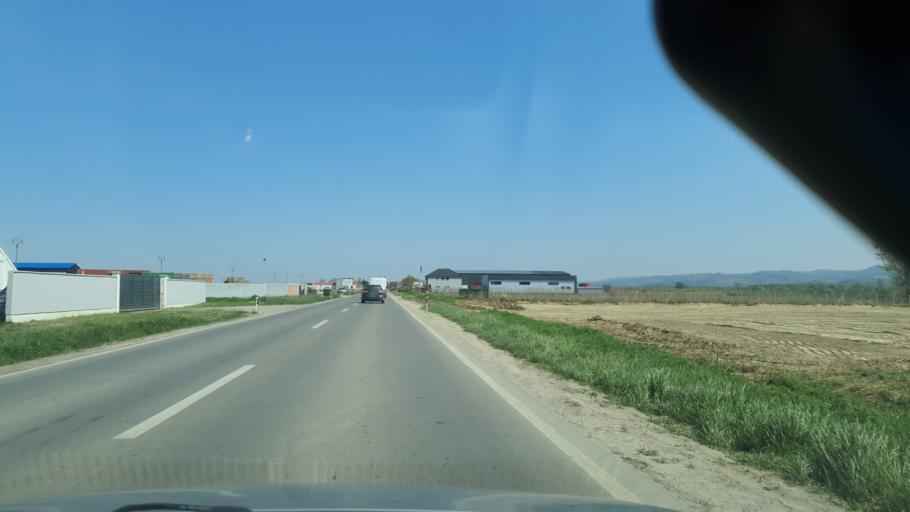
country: RS
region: Autonomna Pokrajina Vojvodina
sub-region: Juznobacki Okrug
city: Beocin
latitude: 45.2406
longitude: 19.6693
